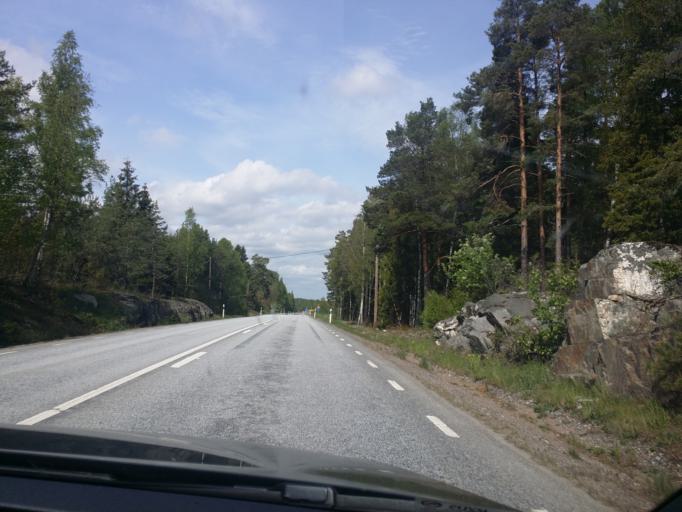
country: SE
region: Uppsala
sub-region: Habo Kommun
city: Balsta
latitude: 59.6394
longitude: 17.5746
